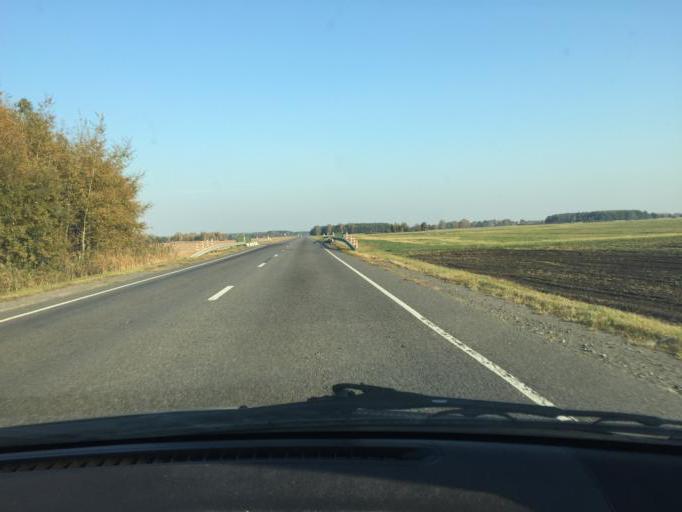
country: BY
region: Brest
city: Davyd-Haradok
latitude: 52.2433
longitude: 27.1675
